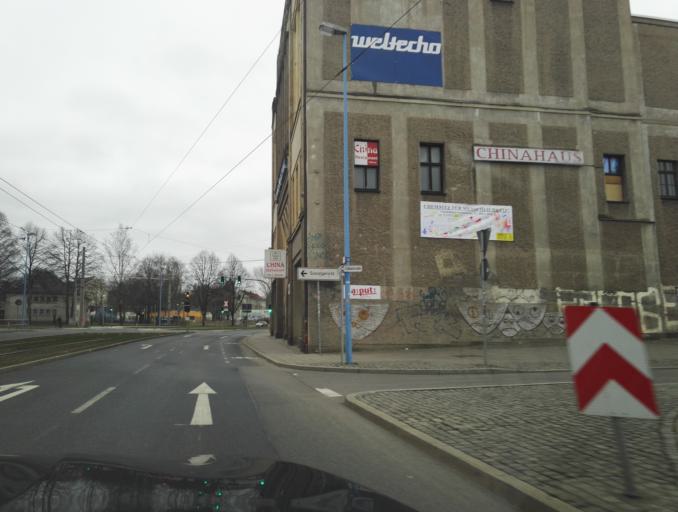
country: DE
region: Saxony
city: Chemnitz
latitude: 50.8289
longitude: 12.9203
